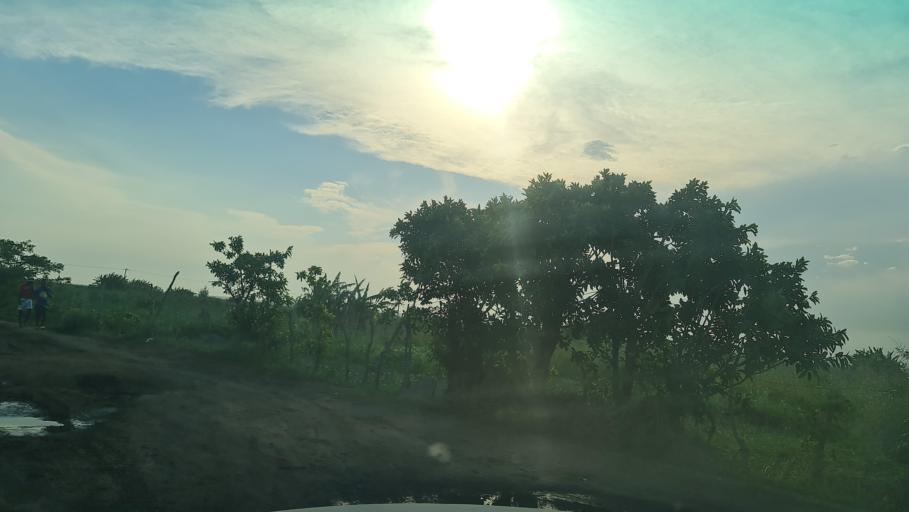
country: MZ
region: Maputo City
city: Maputo
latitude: -25.7374
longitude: 32.7305
